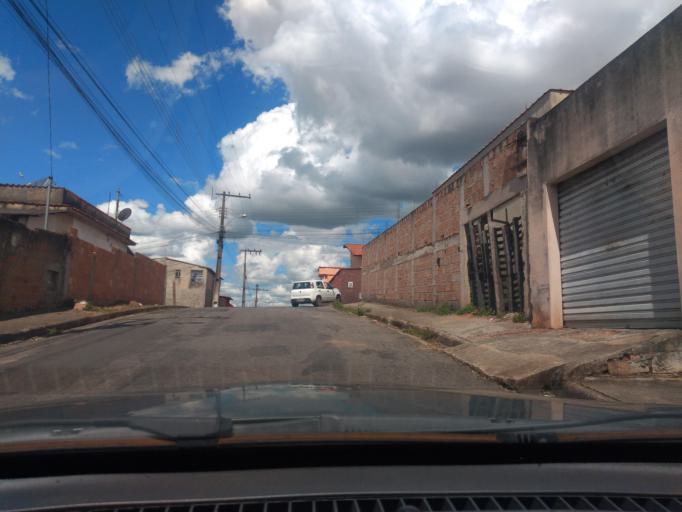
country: BR
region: Minas Gerais
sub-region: Tres Coracoes
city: Tres Coracoes
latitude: -21.6827
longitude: -45.2508
